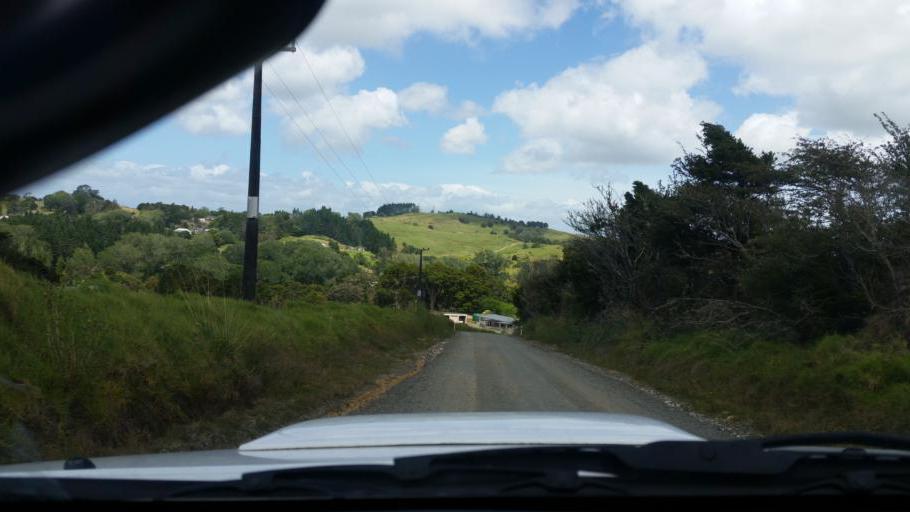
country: NZ
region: Northland
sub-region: Whangarei
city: Ruakaka
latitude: -36.0959
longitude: 174.2309
